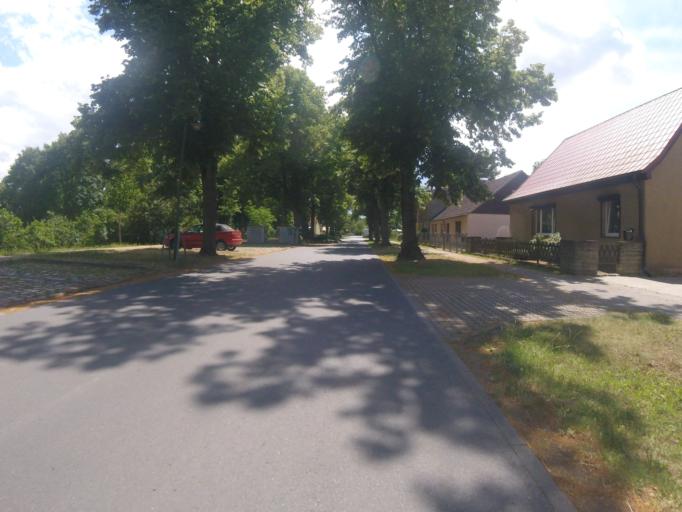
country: DE
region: Brandenburg
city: Bestensee
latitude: 52.2737
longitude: 13.6413
